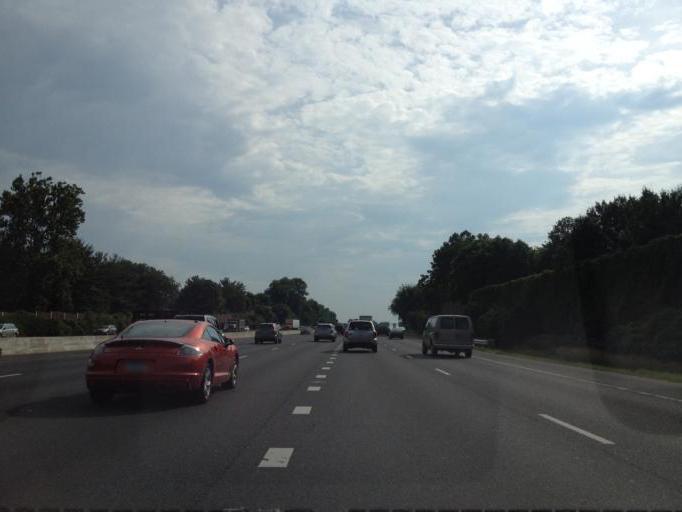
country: US
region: Maryland
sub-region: Baltimore County
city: Mays Chapel
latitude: 39.4170
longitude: -76.6572
